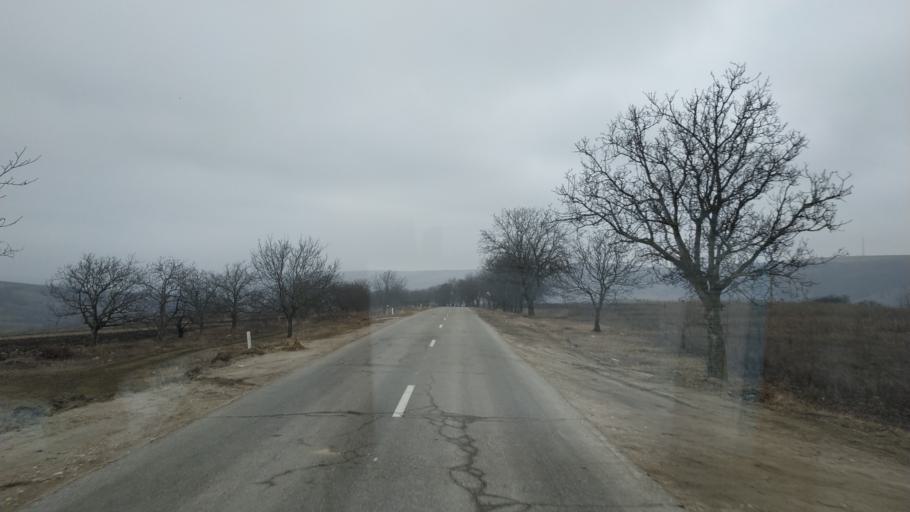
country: MD
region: Stinga Nistrului
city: Bucovat
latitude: 47.0037
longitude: 28.4373
